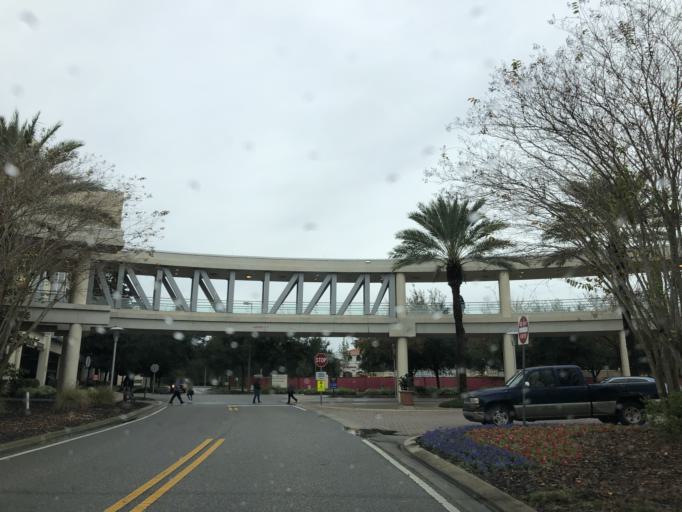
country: US
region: Florida
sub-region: Orange County
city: Doctor Phillips
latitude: 28.4285
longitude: -81.4793
